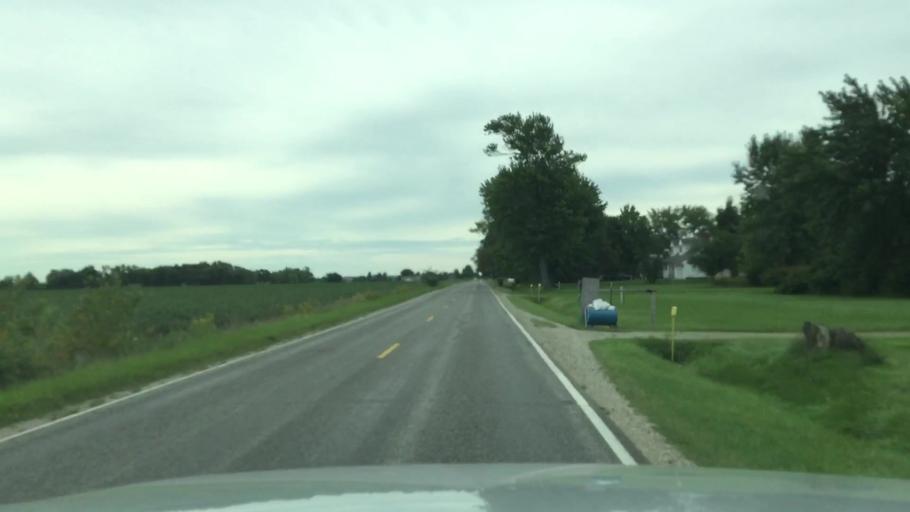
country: US
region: Michigan
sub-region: Shiawassee County
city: Durand
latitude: 43.0468
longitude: -83.9874
